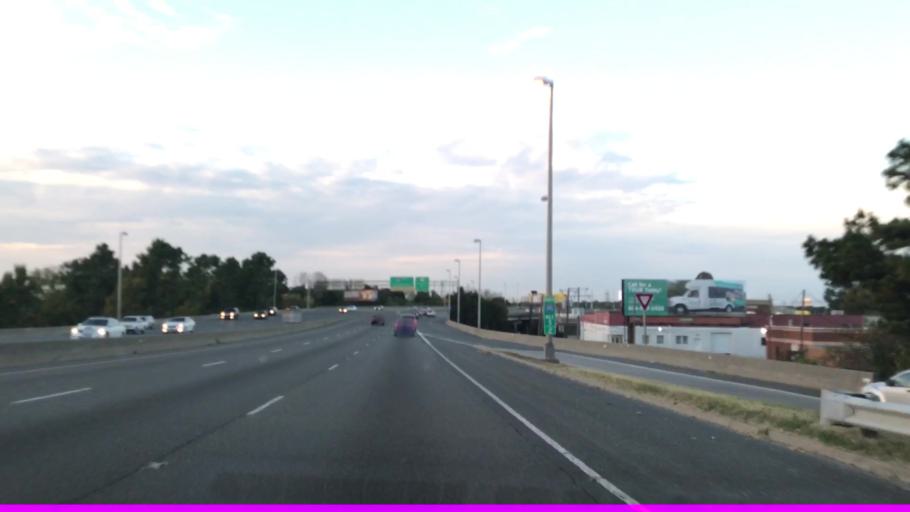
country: US
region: Virginia
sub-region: City of Richmond
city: Richmond
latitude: 37.5740
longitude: -77.4767
